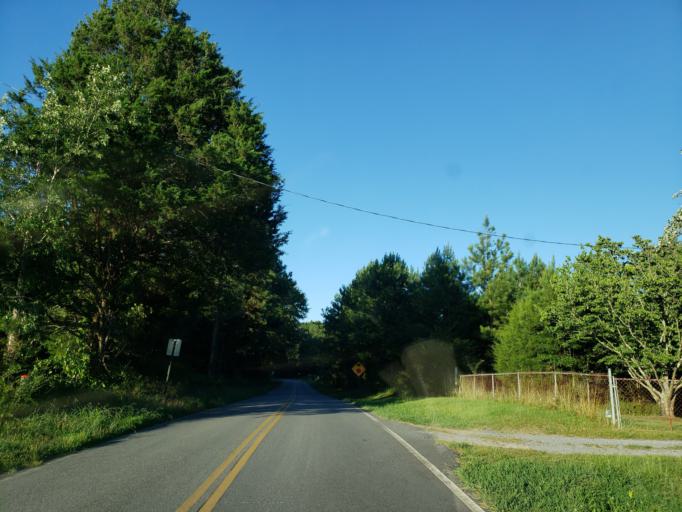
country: US
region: Georgia
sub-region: Polk County
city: Aragon
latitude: 34.1003
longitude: -85.0082
